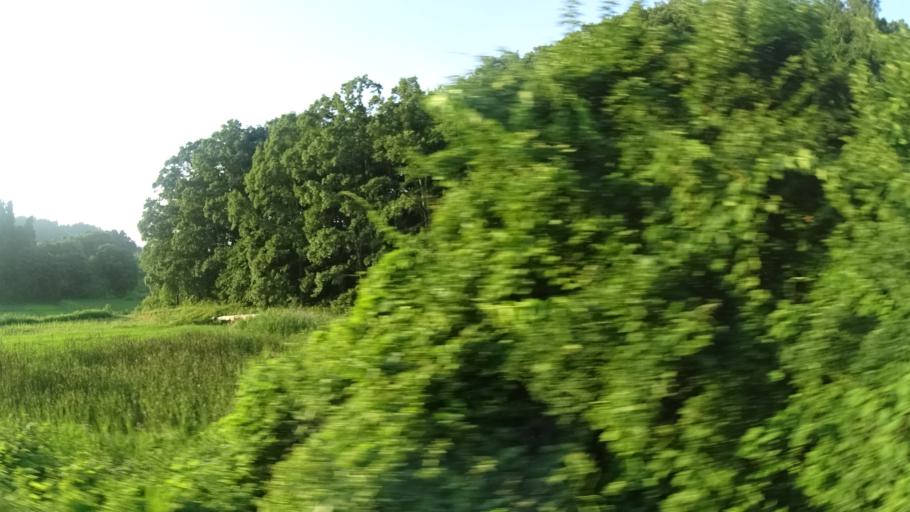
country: JP
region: Fukushima
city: Funehikimachi-funehiki
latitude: 37.4494
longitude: 140.5611
